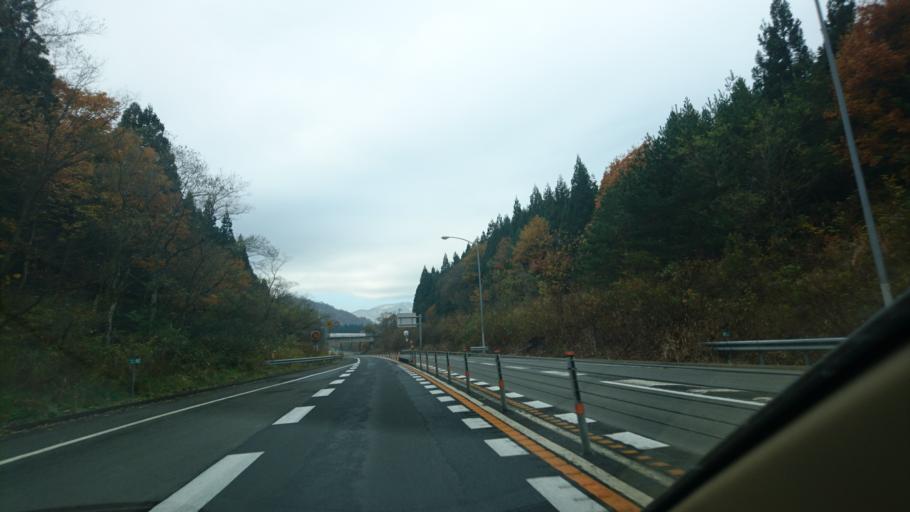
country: JP
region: Iwate
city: Kitakami
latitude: 39.2925
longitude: 140.9815
